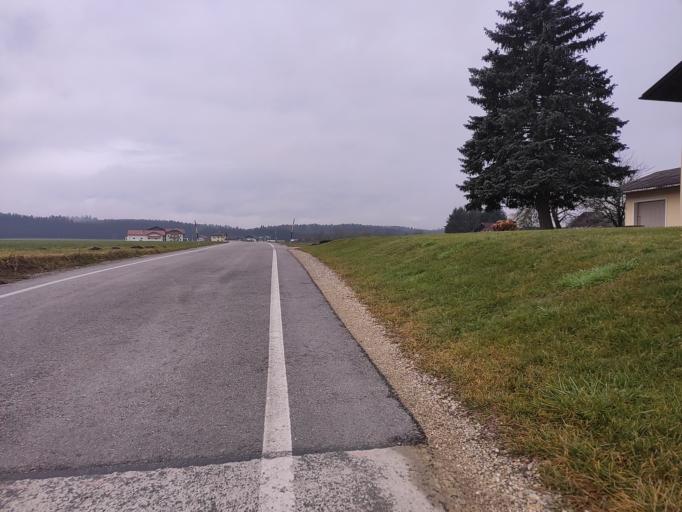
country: AT
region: Salzburg
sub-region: Politischer Bezirk Salzburg-Umgebung
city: Strasswalchen
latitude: 47.9762
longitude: 13.2422
